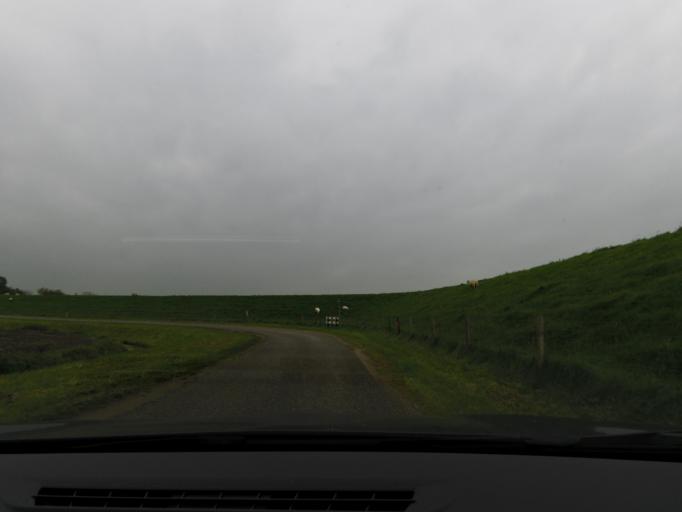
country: NL
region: South Holland
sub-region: Gemeente Goeree-Overflakkee
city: Middelharnis
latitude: 51.7971
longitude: 4.2421
